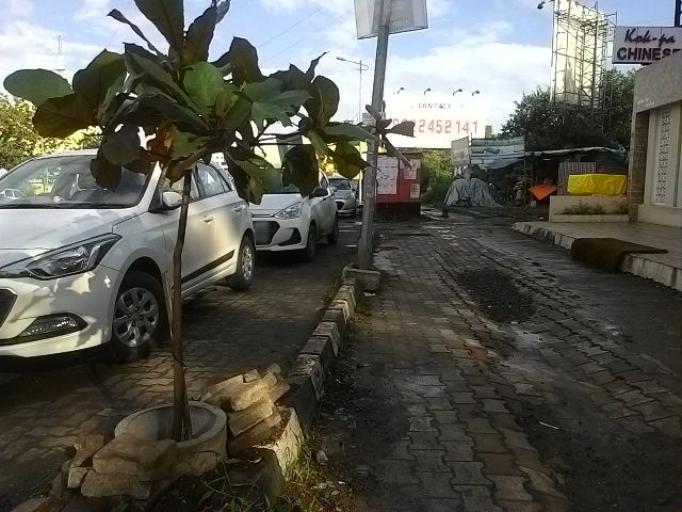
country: IN
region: Maharashtra
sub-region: Pune Division
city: Khadki
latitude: 18.5555
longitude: 73.7951
